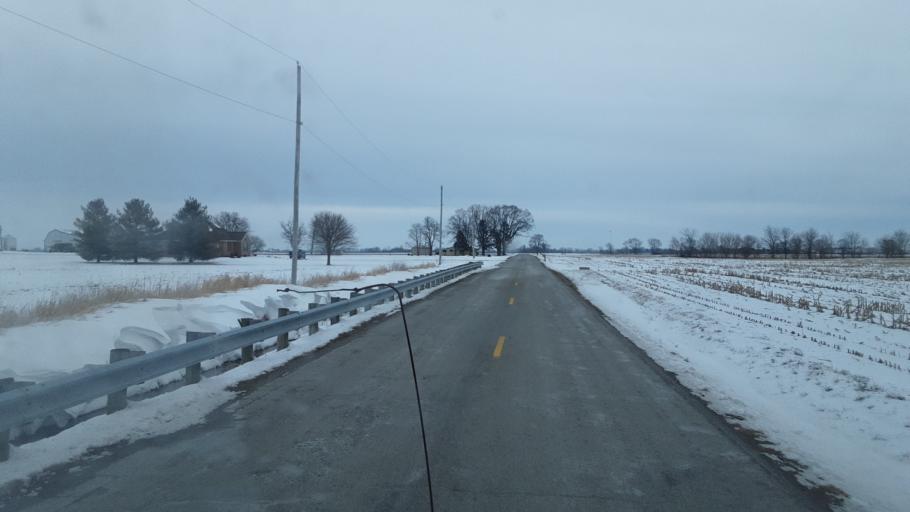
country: US
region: Ohio
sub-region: Madison County
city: Mount Sterling
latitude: 39.7201
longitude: -83.2950
